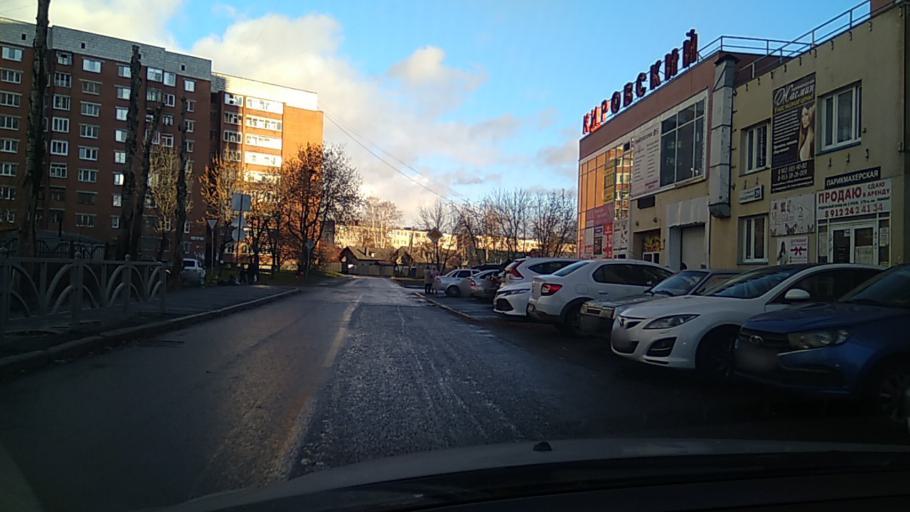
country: RU
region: Sverdlovsk
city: Sovkhoznyy
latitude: 56.7643
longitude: 60.5987
